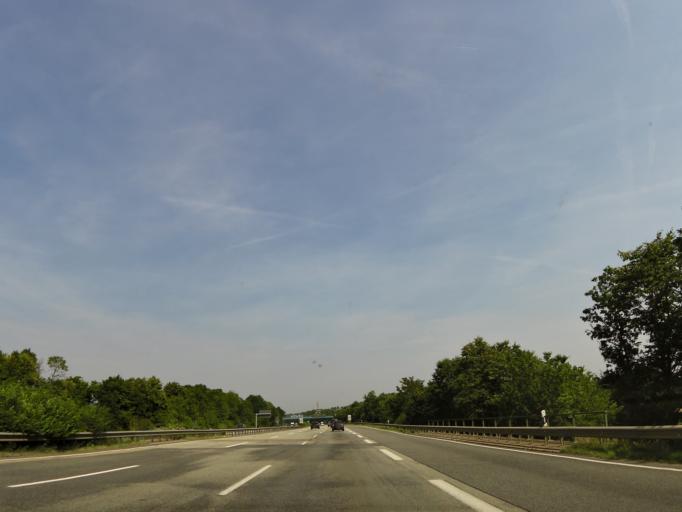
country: DE
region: Rheinland-Pfalz
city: Wehr
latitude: 50.4129
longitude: 7.2358
